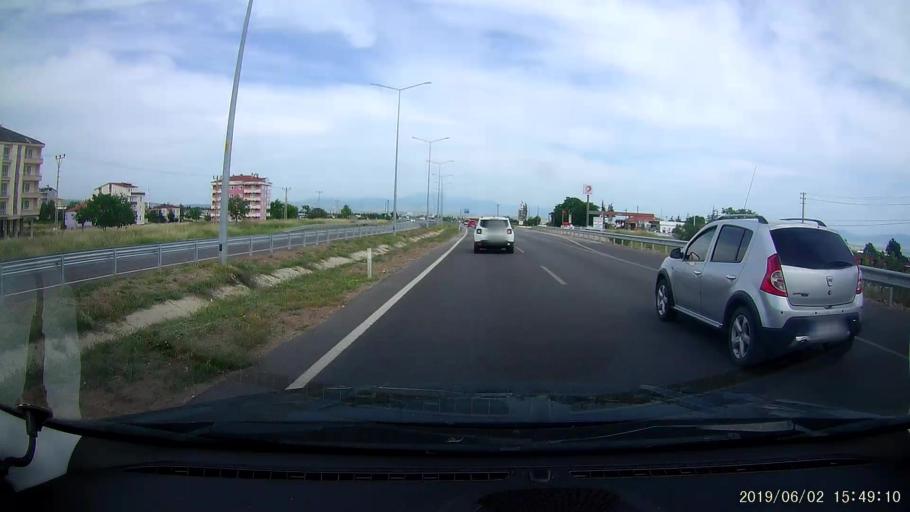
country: TR
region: Amasya
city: Merzifon
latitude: 40.8581
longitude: 35.4587
